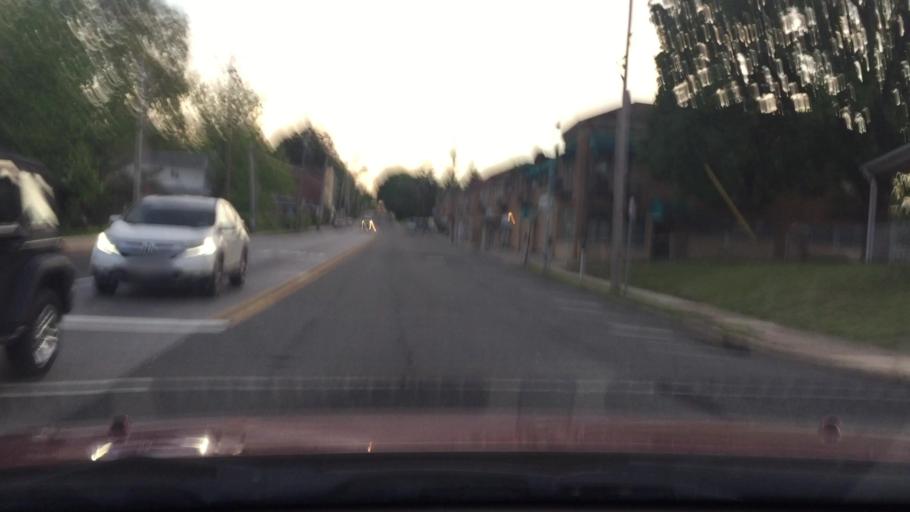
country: US
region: Pennsylvania
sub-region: Delaware County
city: Drexel Hill
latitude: 39.9515
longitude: -75.2822
